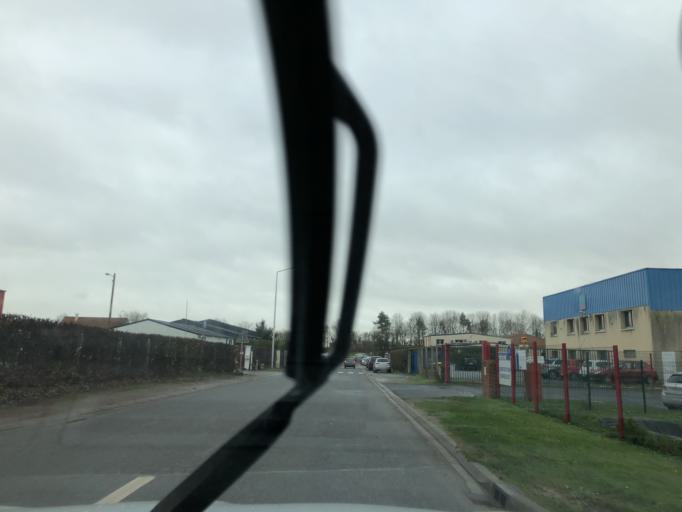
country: FR
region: Lower Normandy
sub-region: Departement du Calvados
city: Giberville
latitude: 49.1694
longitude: -0.2881
